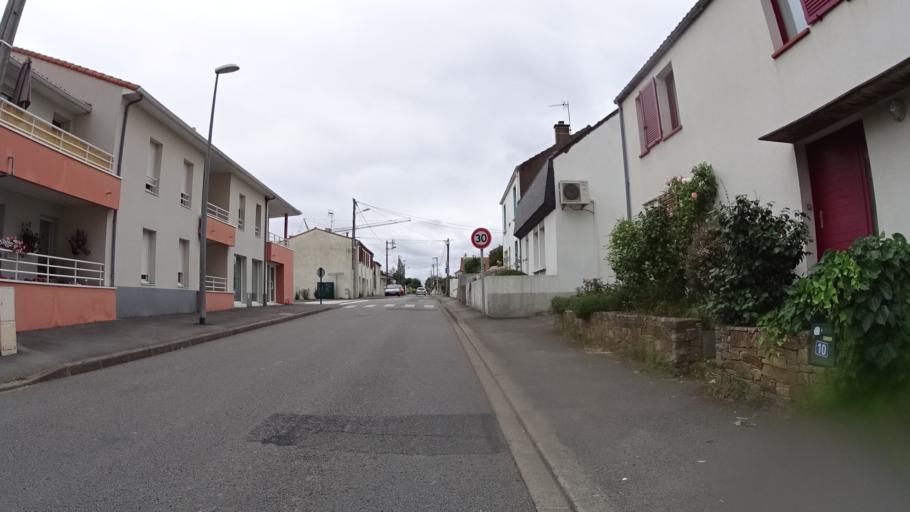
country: FR
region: Pays de la Loire
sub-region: Departement de la Loire-Atlantique
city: Bouguenais
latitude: 47.1783
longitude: -1.6217
